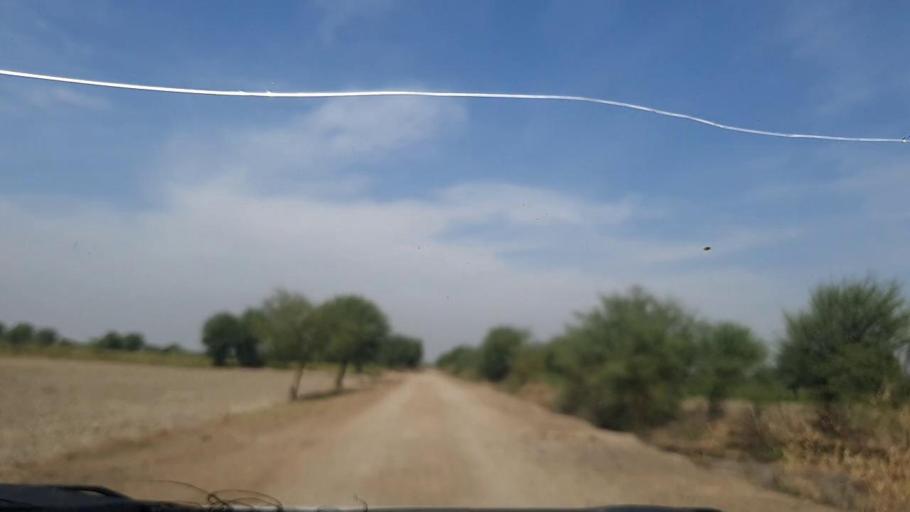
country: PK
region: Sindh
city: Pithoro
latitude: 25.5027
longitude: 69.4591
